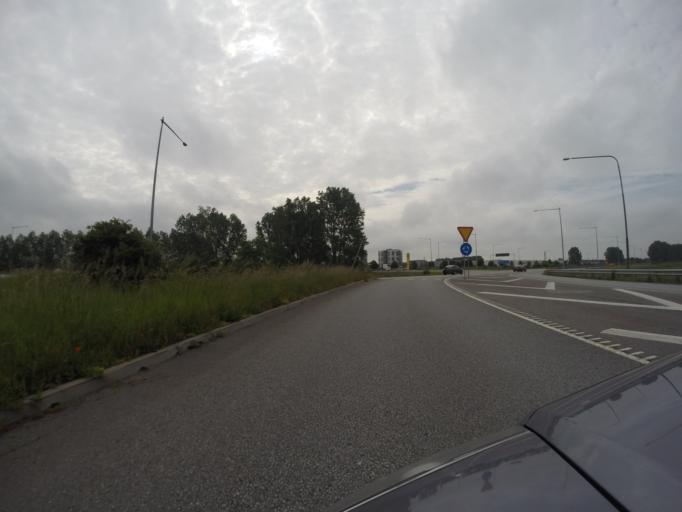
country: SE
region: Skane
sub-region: Burlovs Kommun
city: Arloev
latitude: 55.6401
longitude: 13.0575
